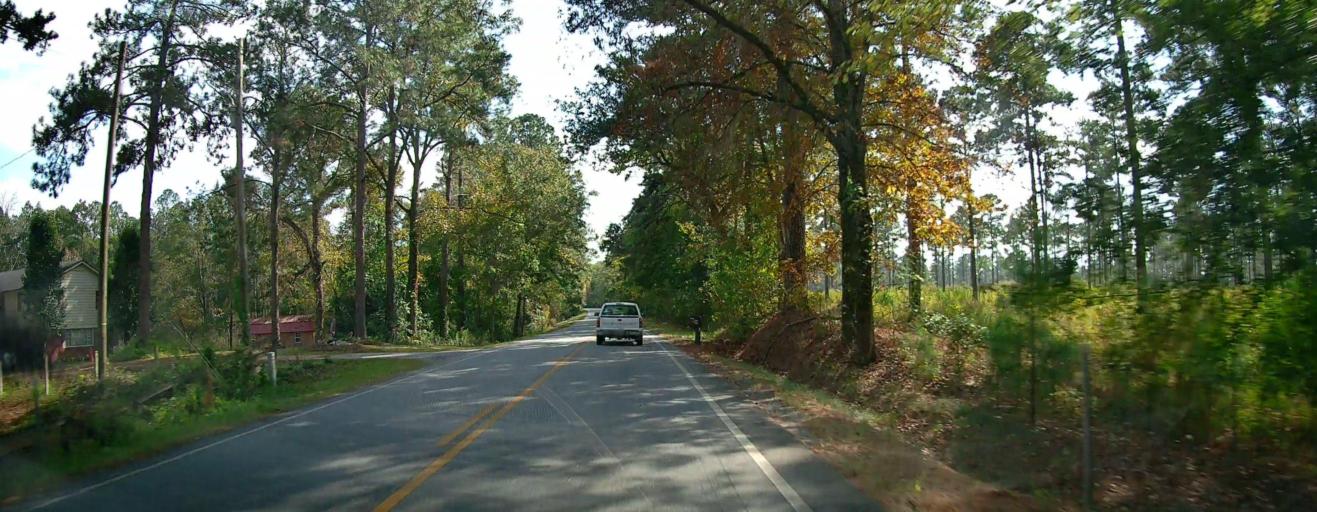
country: US
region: Georgia
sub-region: Thomas County
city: Thomasville
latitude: 30.8950
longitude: -84.0065
